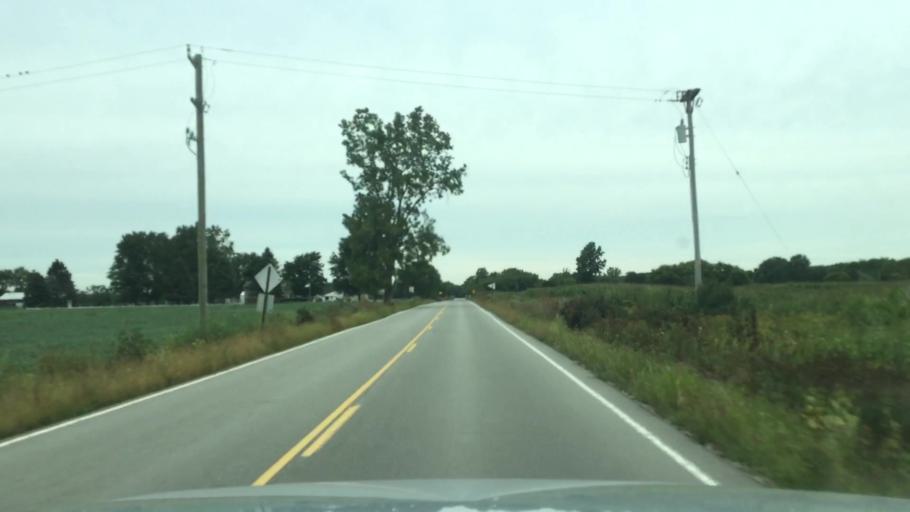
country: US
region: Michigan
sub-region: Washtenaw County
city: Milan
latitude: 42.0862
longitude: -83.7350
